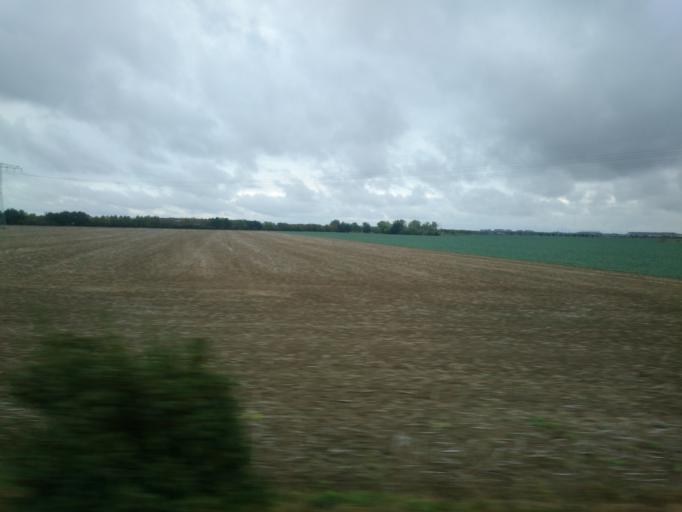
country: DE
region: Saxony-Anhalt
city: Ermlitz
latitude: 51.4053
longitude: 12.1692
